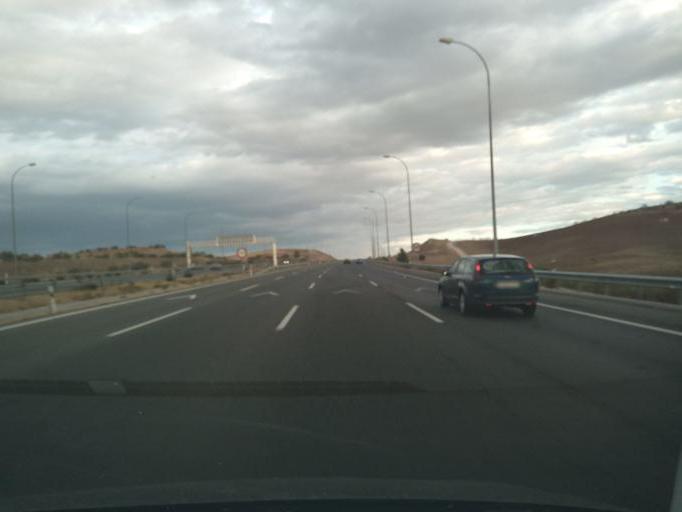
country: ES
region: Madrid
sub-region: Provincia de Madrid
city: Paracuellos de Jarama
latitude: 40.5379
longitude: -3.5290
